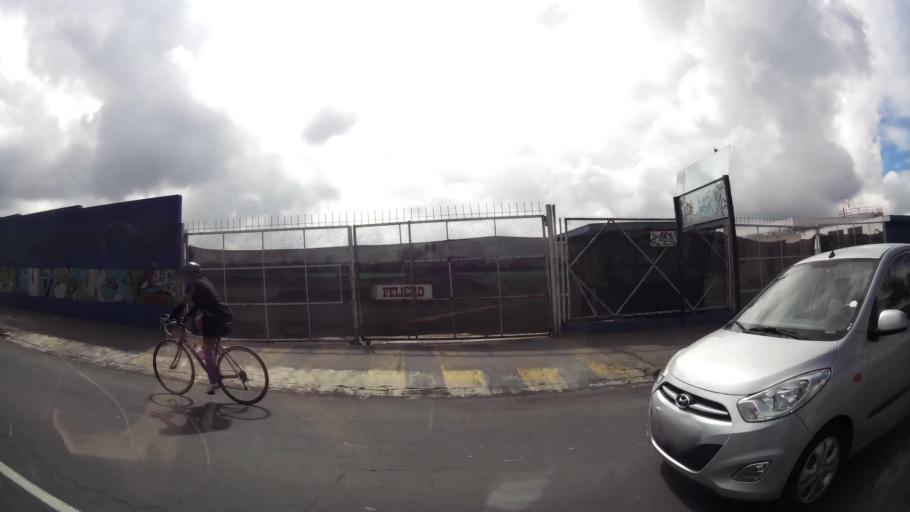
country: EC
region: Pichincha
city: Quito
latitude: -0.1508
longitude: -78.4889
